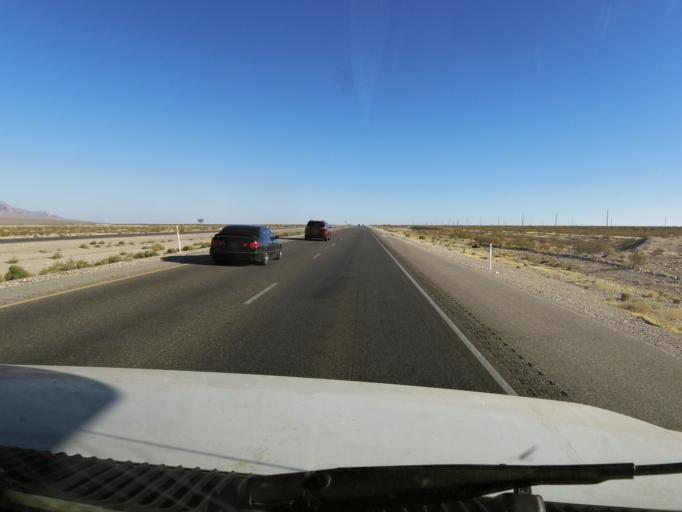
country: US
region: Nevada
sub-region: Clark County
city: Summerlin South
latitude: 36.3984
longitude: -115.3954
